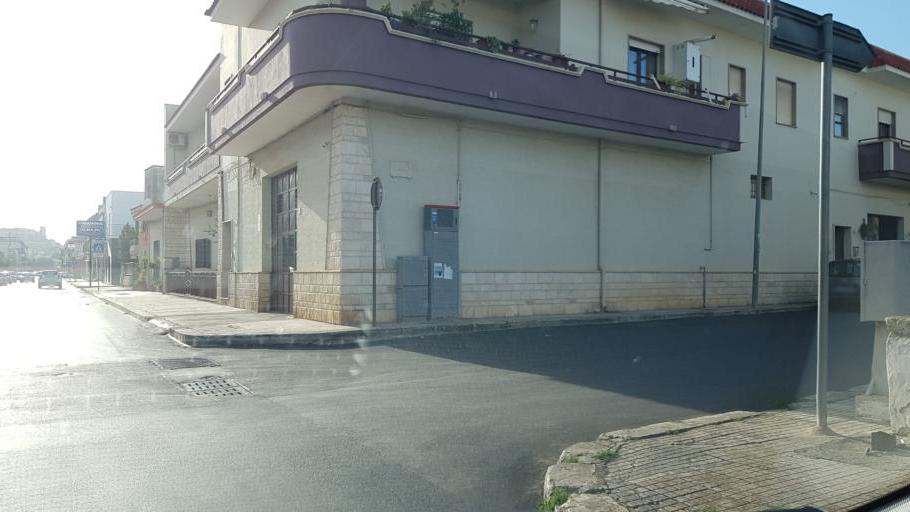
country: IT
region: Apulia
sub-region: Provincia di Brindisi
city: Oria
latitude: 40.5054
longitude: 17.6512
